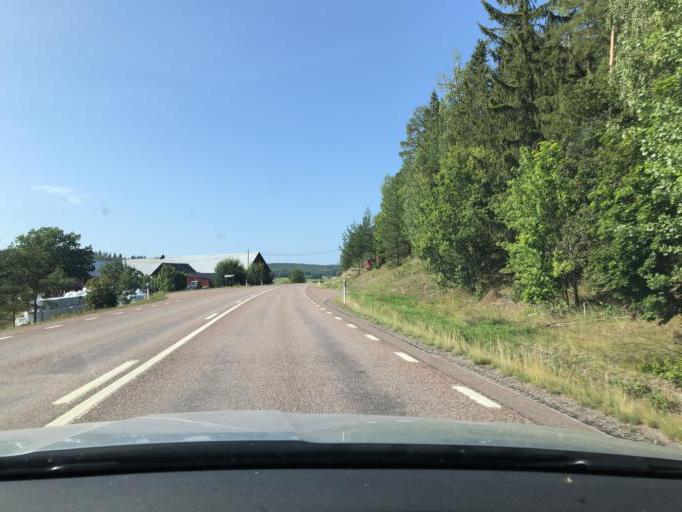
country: SE
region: Dalarna
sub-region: Saters Kommun
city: Saeter
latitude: 60.4348
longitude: 15.8265
